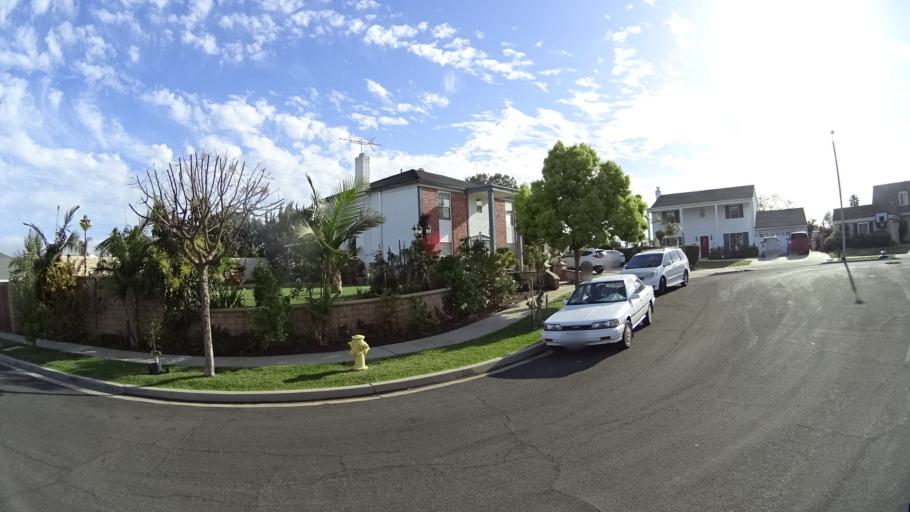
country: US
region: California
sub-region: Ventura County
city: Casa Conejo
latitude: 34.1770
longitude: -118.9500
